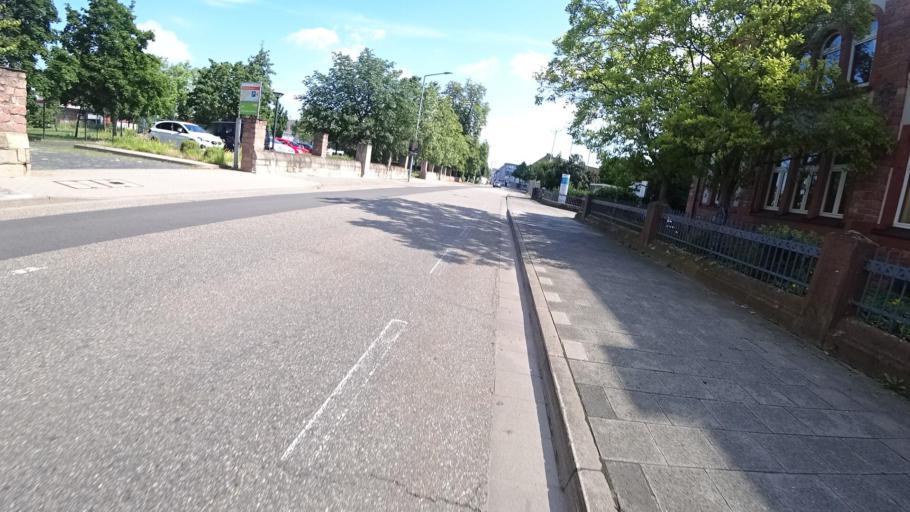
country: DE
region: Rheinland-Pfalz
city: Worms
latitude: 49.6249
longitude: 8.3626
